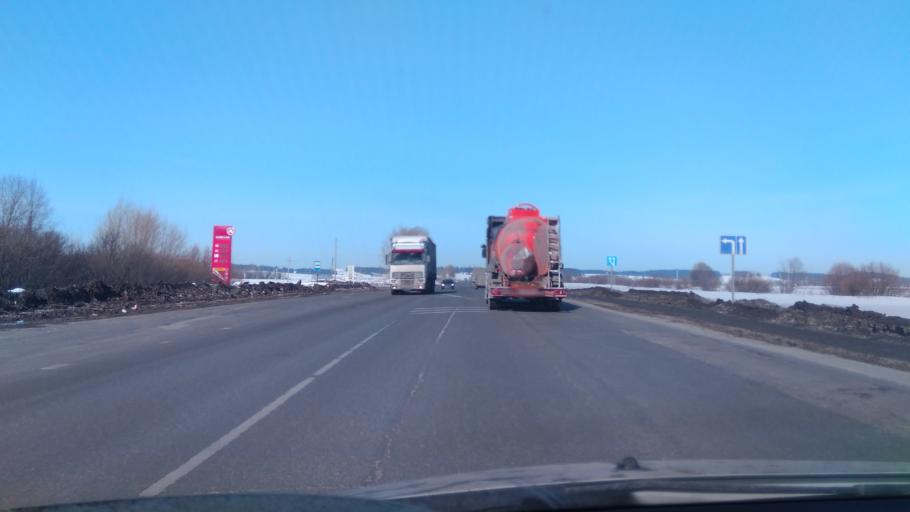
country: RU
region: Perm
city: Kukushtan
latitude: 57.5033
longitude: 56.6522
